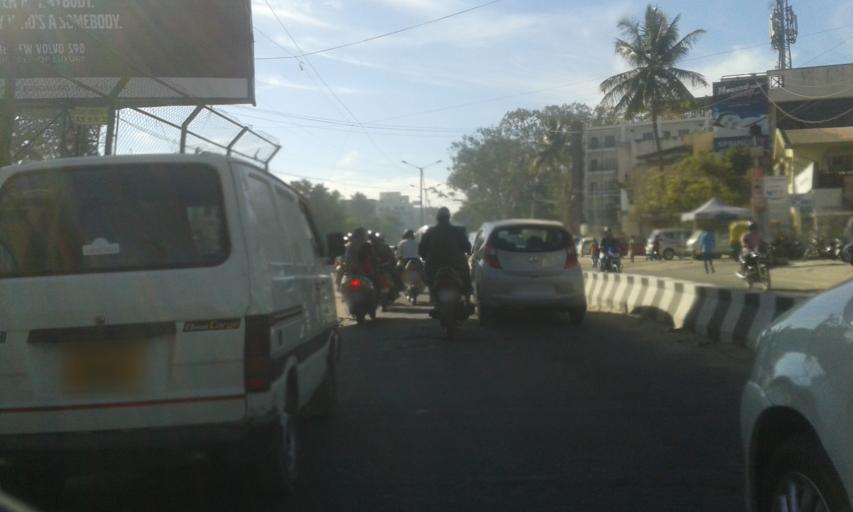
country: IN
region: Karnataka
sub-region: Bangalore Urban
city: Bangalore
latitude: 12.9498
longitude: 77.6060
